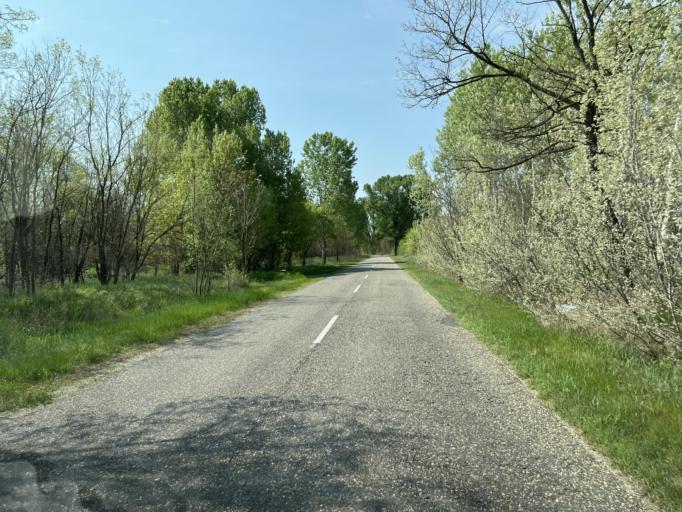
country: HU
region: Pest
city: Kocser
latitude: 47.0670
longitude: 19.8637
